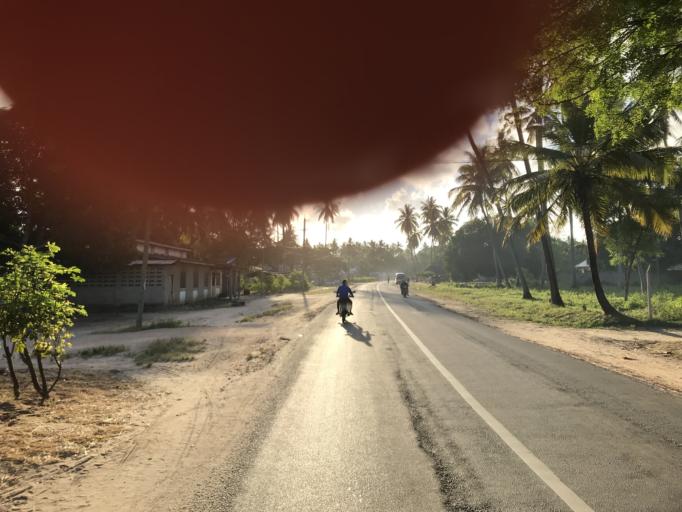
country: TZ
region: Dar es Salaam
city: Dar es Salaam
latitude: -6.8640
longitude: 39.3619
